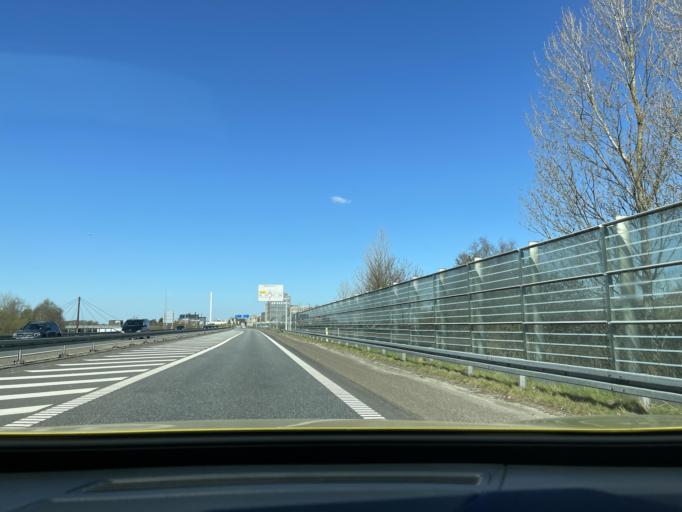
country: DK
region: Central Jutland
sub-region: Herning Kommune
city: Herning
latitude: 56.1302
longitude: 8.9964
